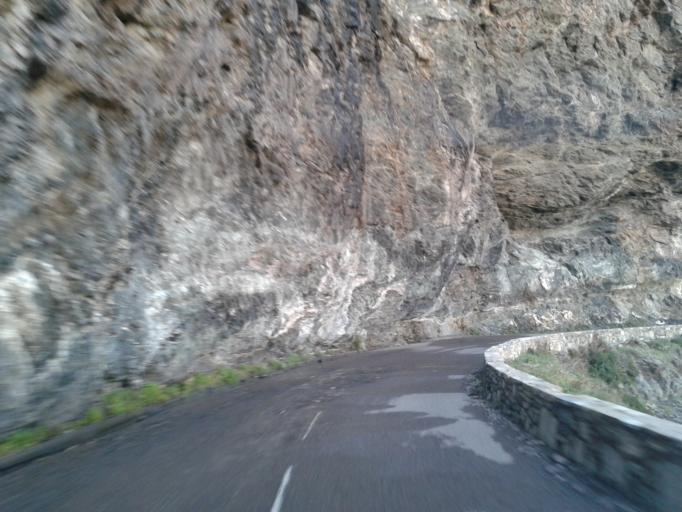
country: FR
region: Corsica
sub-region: Departement de la Haute-Corse
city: Saint-Florent
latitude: 42.7632
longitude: 9.3389
